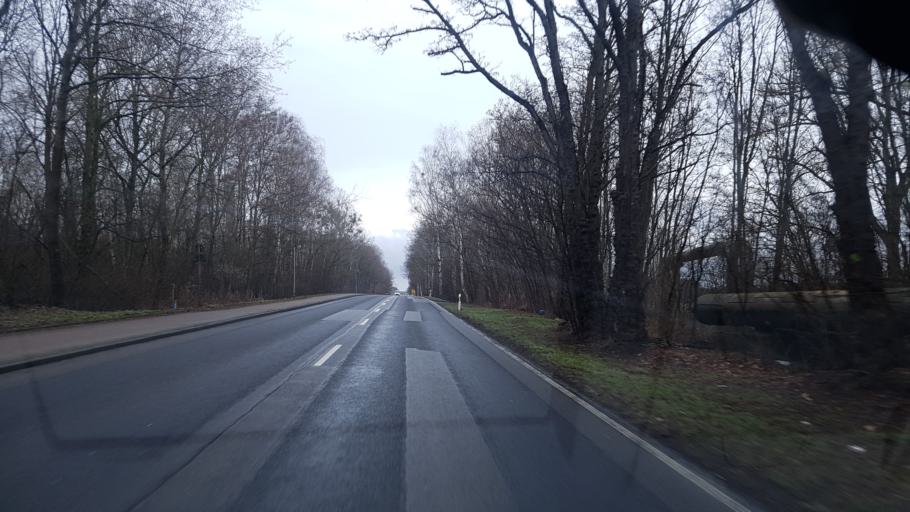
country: DE
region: Brandenburg
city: Grossraschen
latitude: 51.5844
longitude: 13.9869
